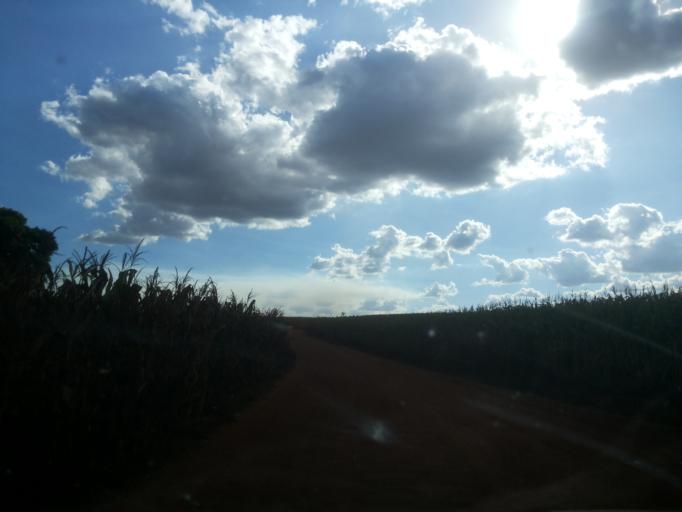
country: BR
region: Minas Gerais
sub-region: Capinopolis
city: Capinopolis
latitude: -18.5831
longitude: -49.4970
